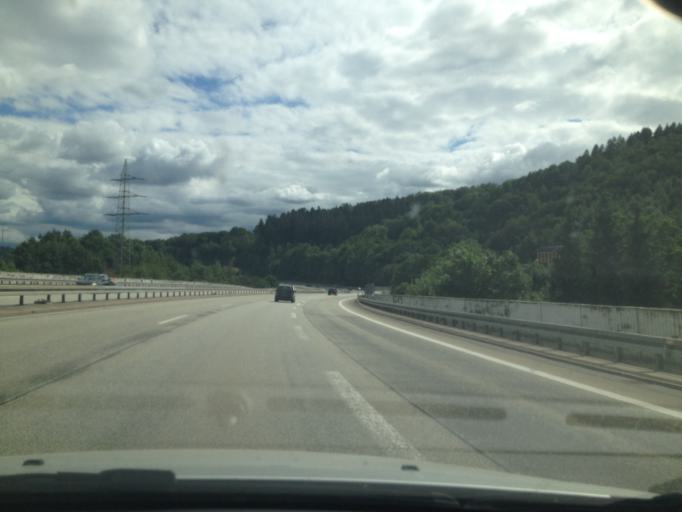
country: DE
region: North Rhine-Westphalia
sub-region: Regierungsbezirk Arnsberg
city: Siegen
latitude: 50.9067
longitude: 8.0159
